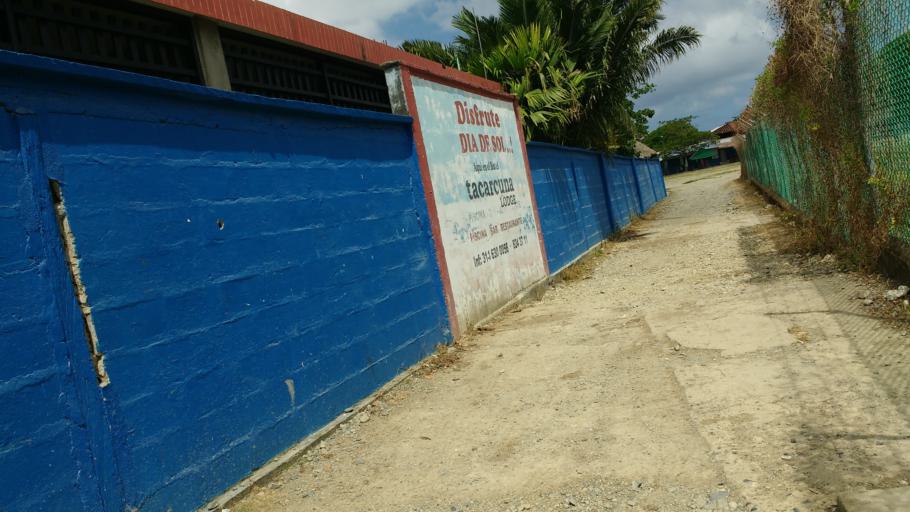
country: PA
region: Guna Yala
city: Puerto Obaldia
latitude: 8.6356
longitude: -77.3482
